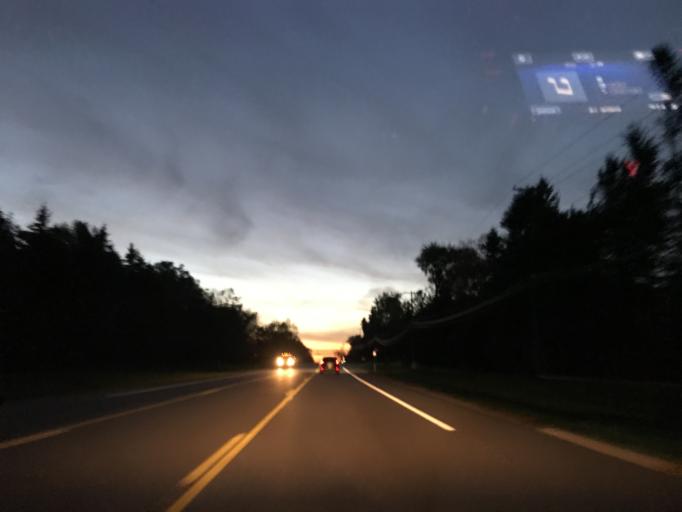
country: US
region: Michigan
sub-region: Wayne County
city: Northville
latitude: 42.4368
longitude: -83.5029
